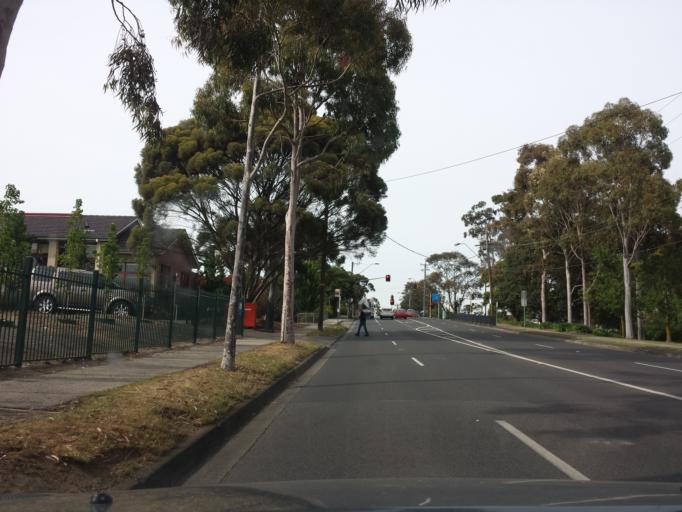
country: AU
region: Victoria
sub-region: Monash
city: Ashwood
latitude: -37.8740
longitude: 145.1294
